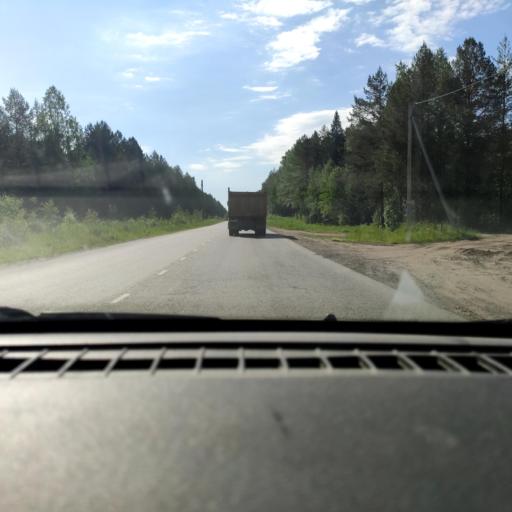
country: RU
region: Perm
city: Overyata
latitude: 58.0176
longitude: 55.8597
